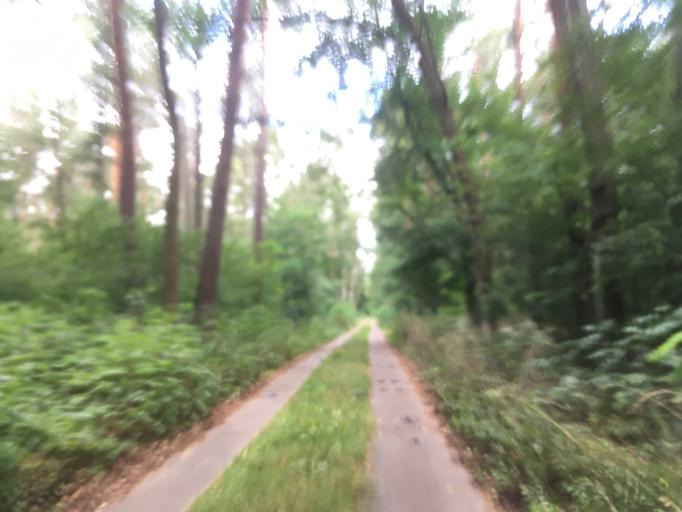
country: DE
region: Berlin
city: Schmockwitz
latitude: 52.3381
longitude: 13.6817
